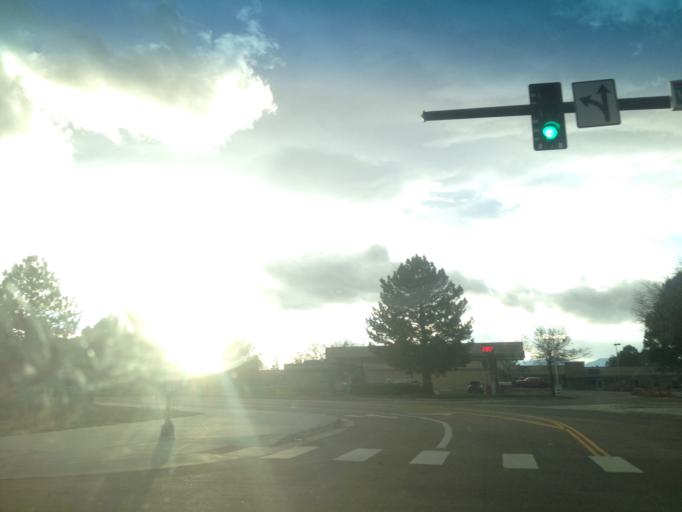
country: US
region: Colorado
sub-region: Adams County
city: Westminster
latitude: 39.8627
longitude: -105.0626
